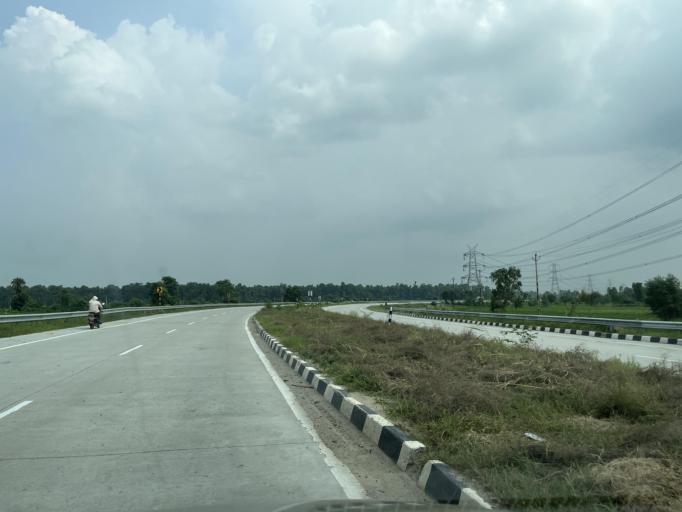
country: IN
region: Uttarakhand
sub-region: Udham Singh Nagar
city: Jaspur
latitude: 29.2807
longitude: 78.8652
